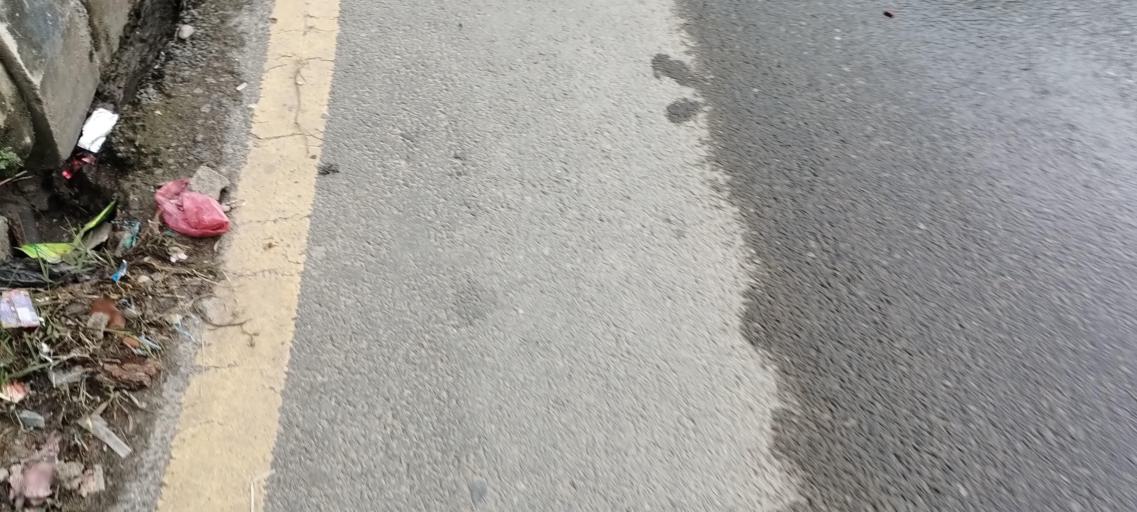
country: NP
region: Central Region
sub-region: Bagmati Zone
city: Kathmandu
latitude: 27.7801
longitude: 85.3635
